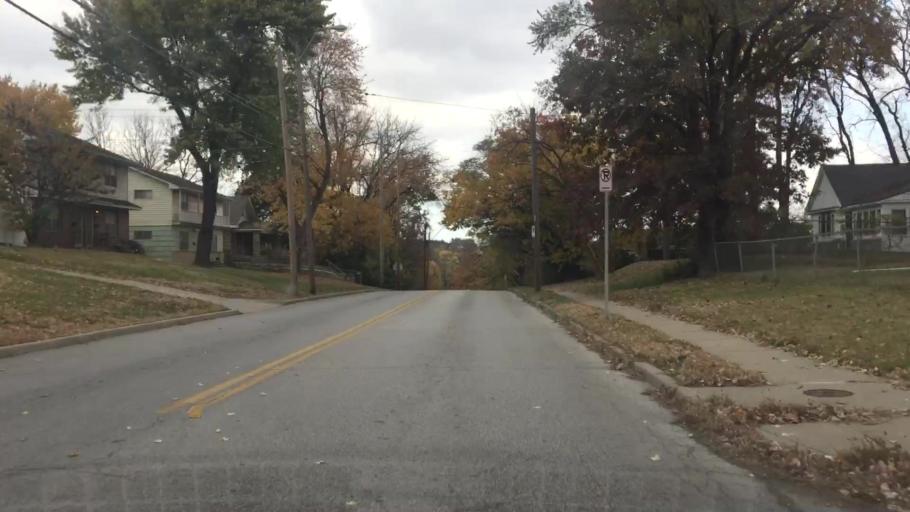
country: US
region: Kansas
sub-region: Johnson County
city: Mission Hills
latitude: 38.9957
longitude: -94.5430
